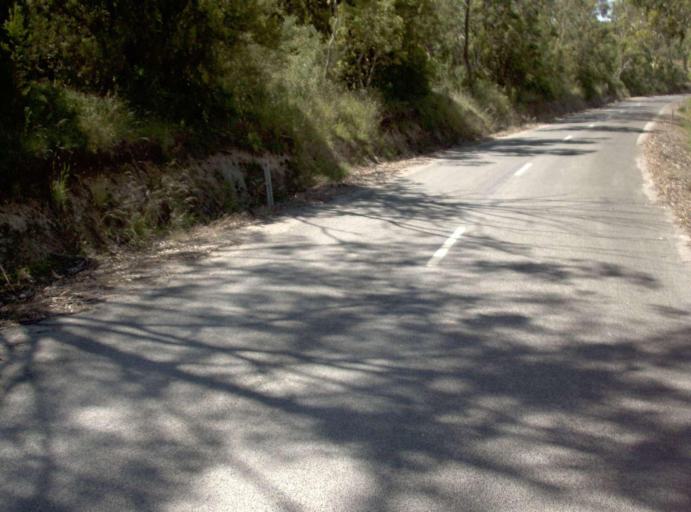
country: AU
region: Victoria
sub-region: East Gippsland
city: Lakes Entrance
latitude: -37.4534
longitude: 148.1921
